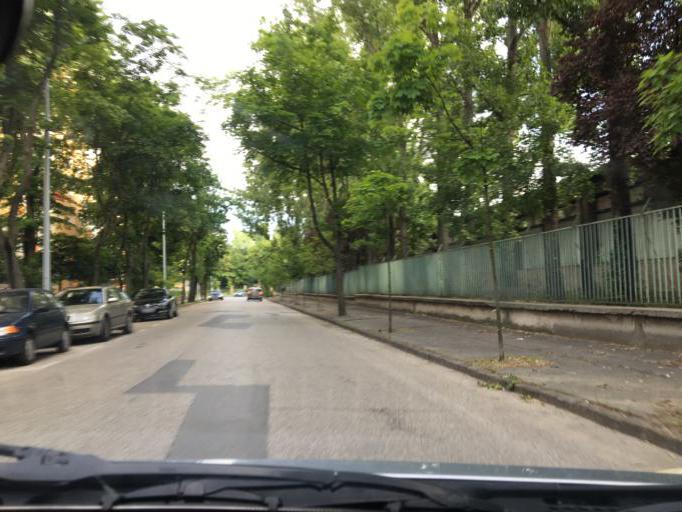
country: HU
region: Budapest
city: Budapest XIII. keruelet
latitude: 47.5236
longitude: 19.0710
